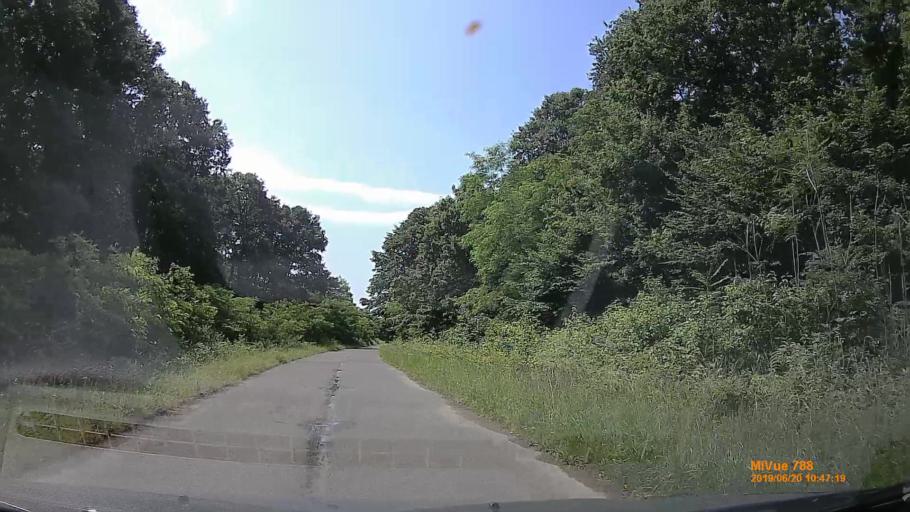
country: HU
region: Baranya
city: Hidas
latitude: 46.1761
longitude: 18.5821
